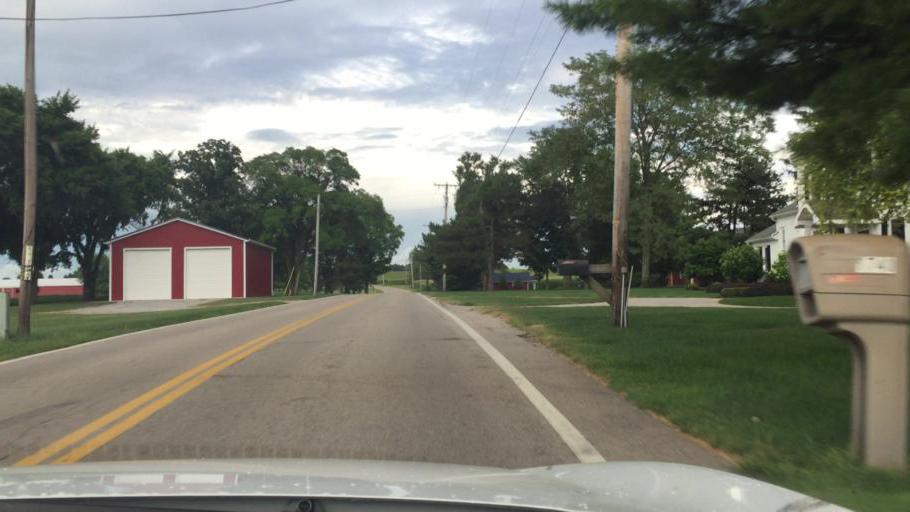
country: US
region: Ohio
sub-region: Clark County
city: Lisbon
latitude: 39.9422
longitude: -83.6384
